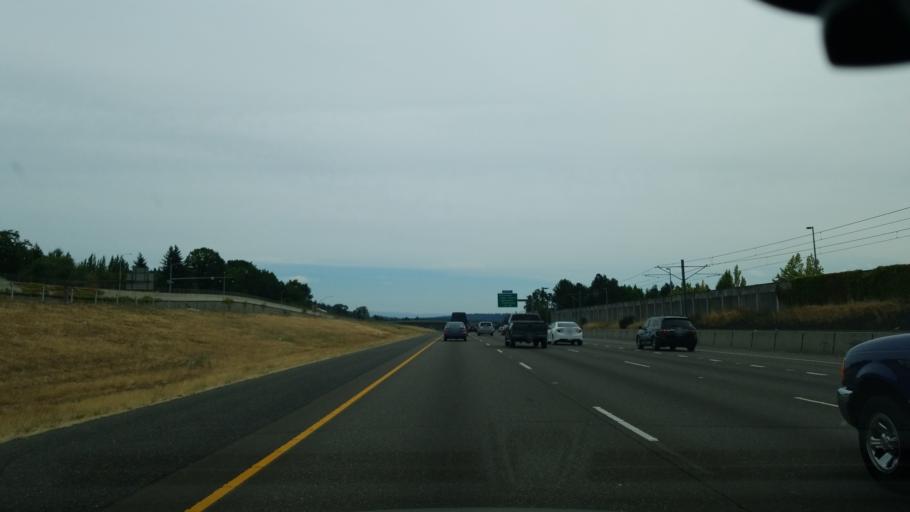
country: US
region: Oregon
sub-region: Clackamas County
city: Clackamas
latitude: 45.4435
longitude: -122.5700
